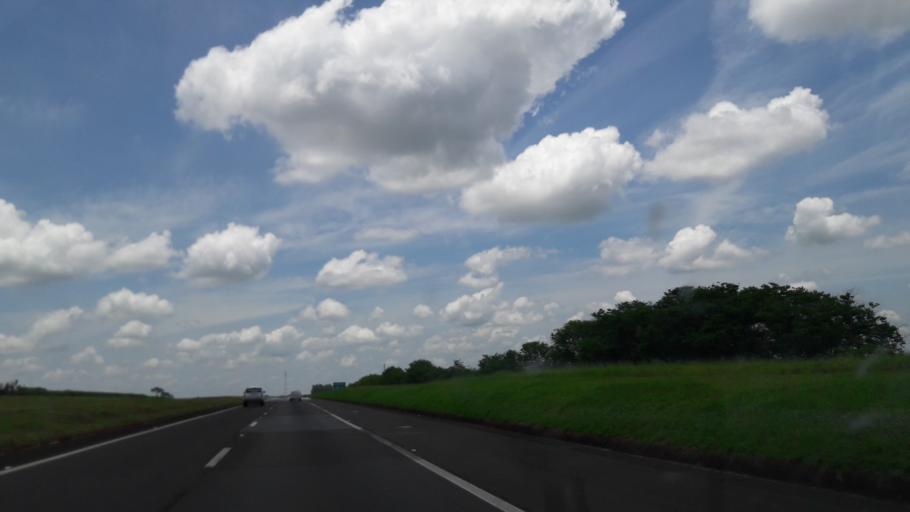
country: BR
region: Sao Paulo
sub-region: Avare
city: Avare
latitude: -22.9562
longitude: -48.8452
